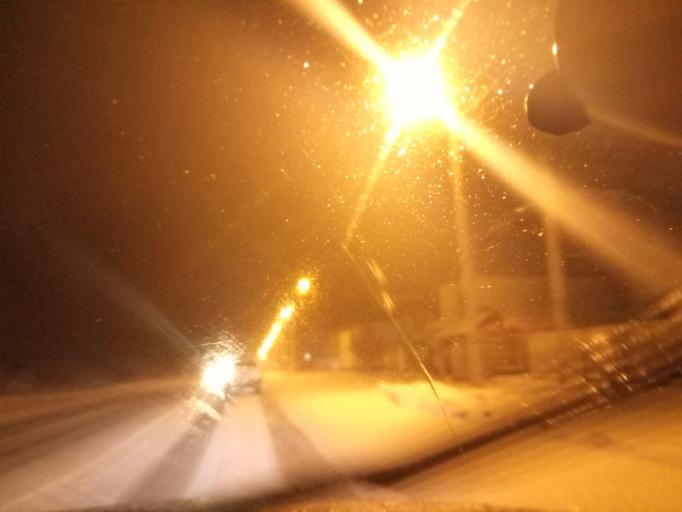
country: RU
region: Tula
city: Novomoskovsk
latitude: 53.9912
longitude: 38.2986
